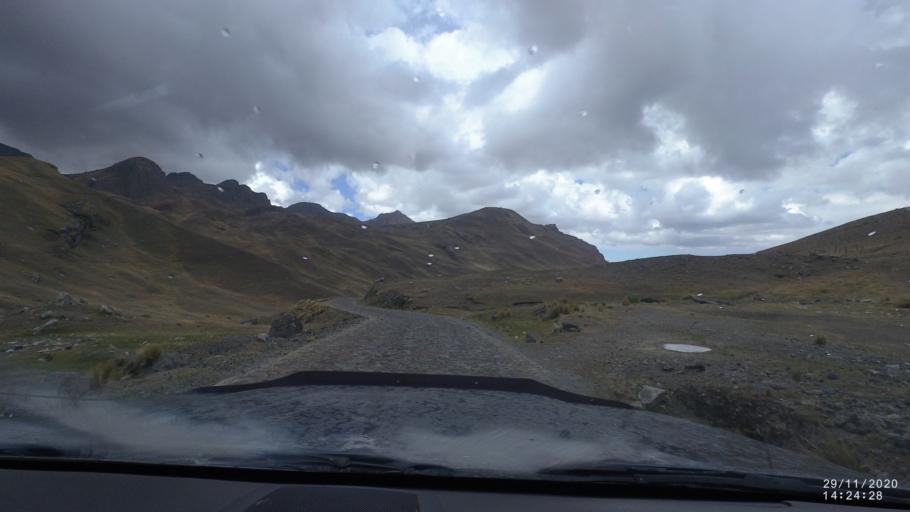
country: BO
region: Cochabamba
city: Sipe Sipe
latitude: -17.2546
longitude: -66.3788
